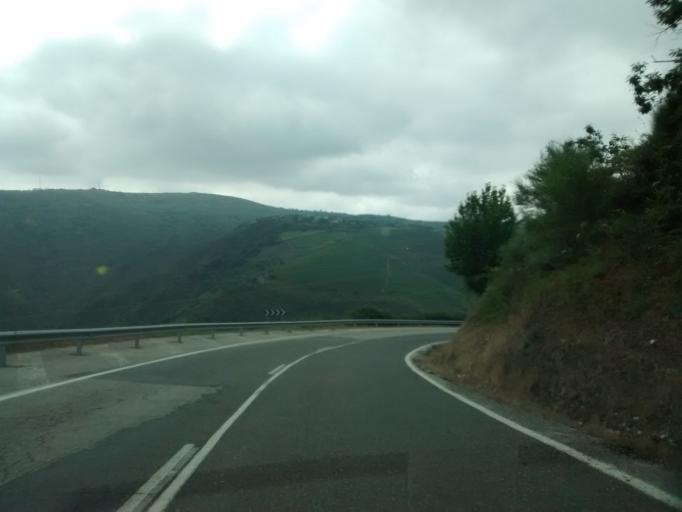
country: ES
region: Galicia
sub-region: Provincia de Ourense
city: Manzaneda
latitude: 42.3275
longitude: -7.2154
